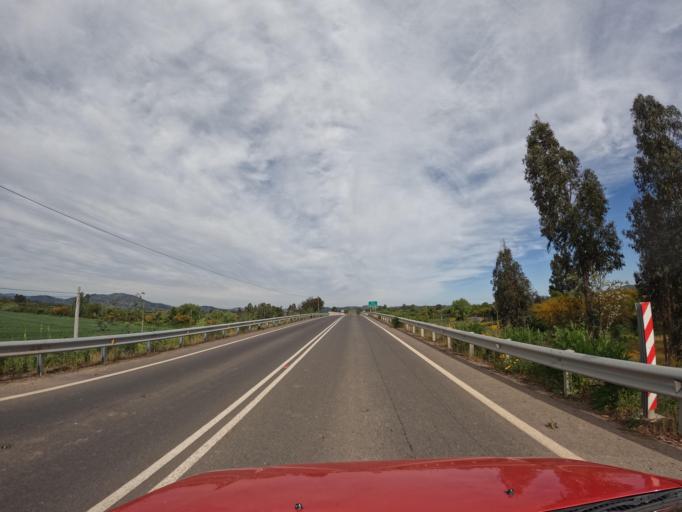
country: CL
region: Maule
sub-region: Provincia de Talca
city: Talca
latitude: -35.3767
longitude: -71.8331
